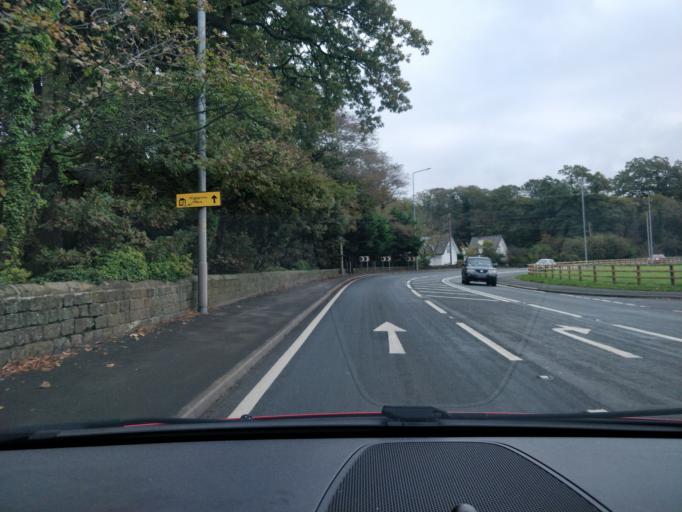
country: GB
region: England
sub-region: Lancashire
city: Ormskirk
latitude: 53.6013
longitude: -2.9274
